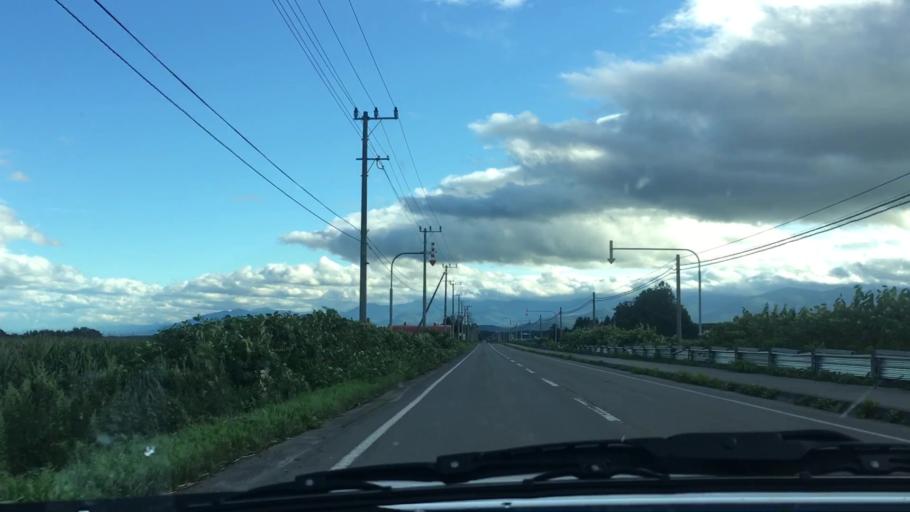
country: JP
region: Hokkaido
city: Otofuke
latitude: 43.1514
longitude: 142.9004
